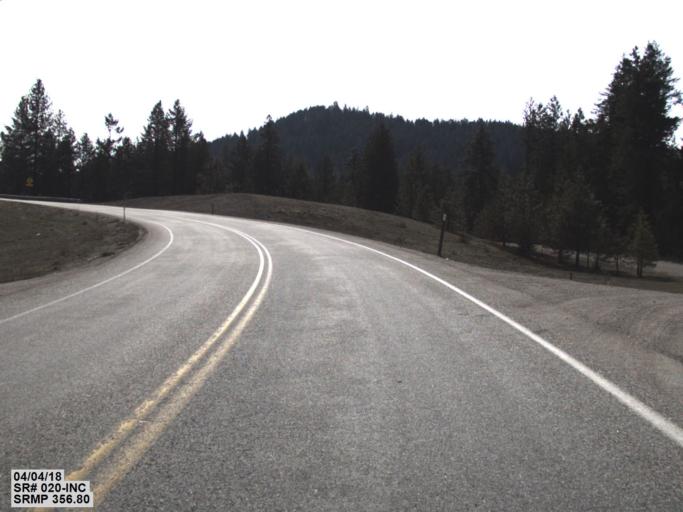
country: US
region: Washington
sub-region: Stevens County
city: Colville
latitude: 48.5449
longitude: -117.8544
